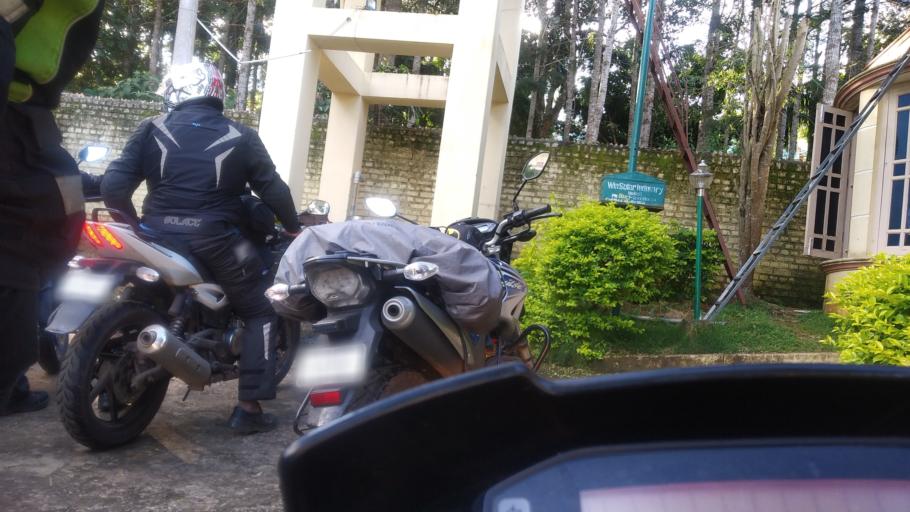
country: IN
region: Tamil Nadu
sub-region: Salem
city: Salem
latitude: 11.7713
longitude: 78.2118
